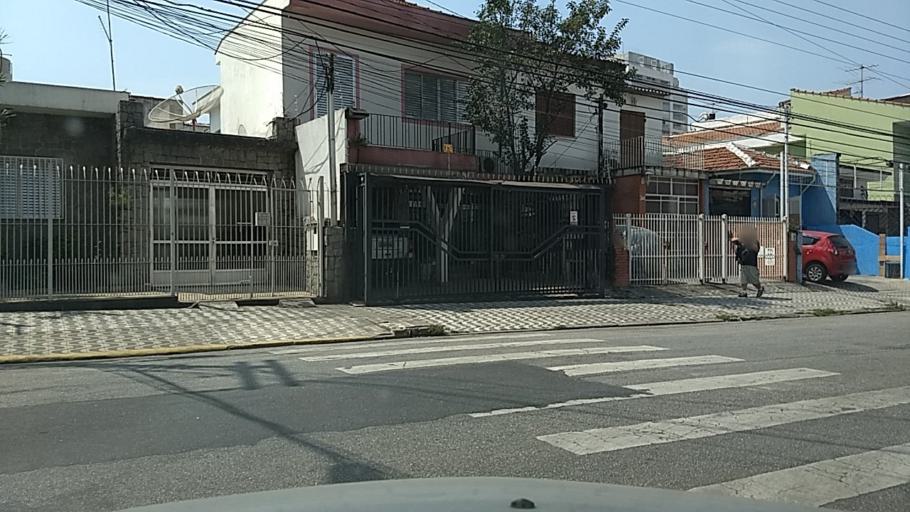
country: BR
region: Sao Paulo
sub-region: Sao Paulo
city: Sao Paulo
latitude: -23.5305
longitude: -46.5640
